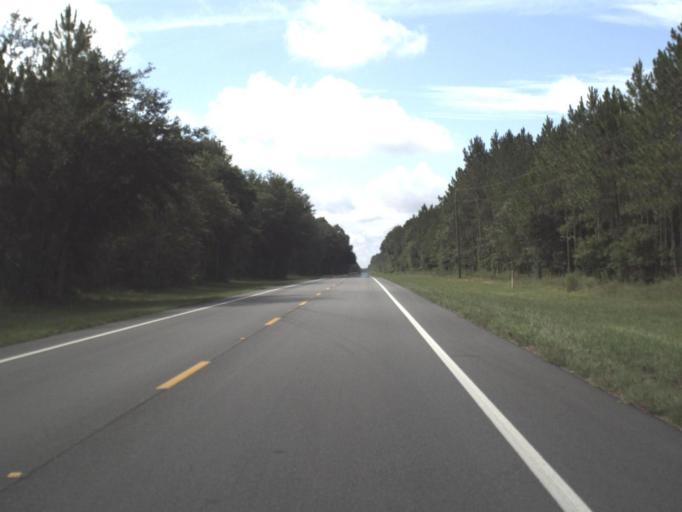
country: US
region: Florida
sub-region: Columbia County
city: Five Points
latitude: 30.4068
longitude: -82.6340
